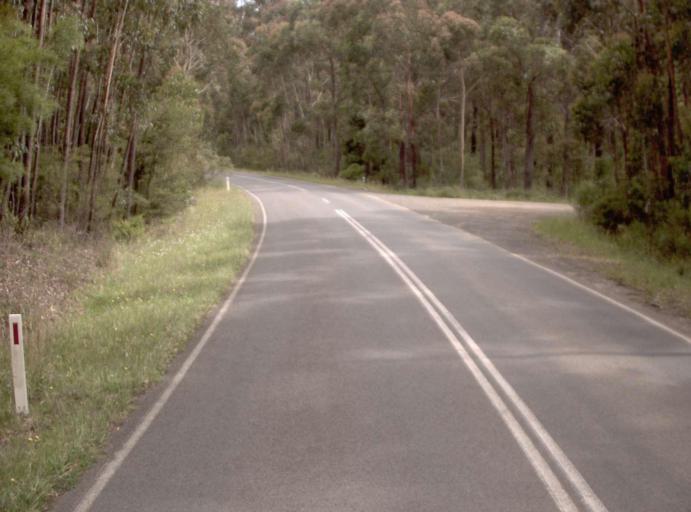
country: AU
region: Victoria
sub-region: Latrobe
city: Traralgon
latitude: -38.0161
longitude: 146.4210
